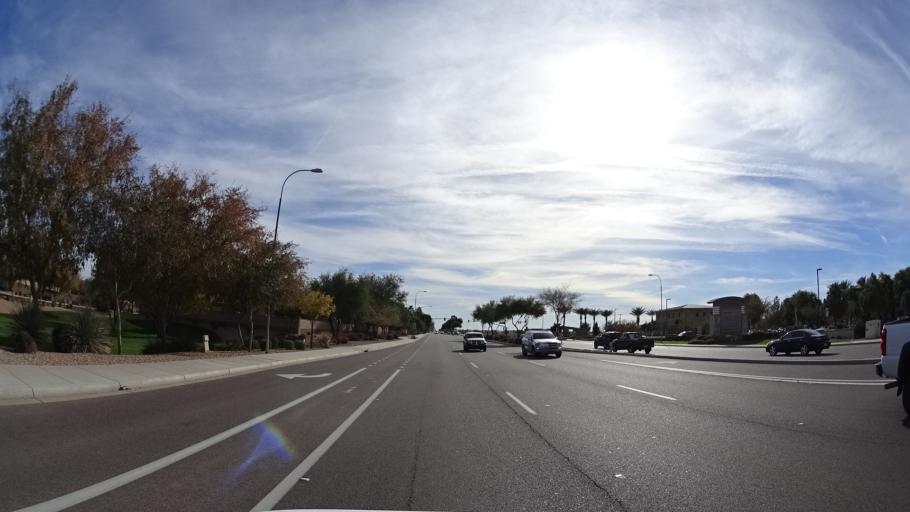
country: US
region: Arizona
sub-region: Maricopa County
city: Chandler
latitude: 33.2716
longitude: -111.7895
